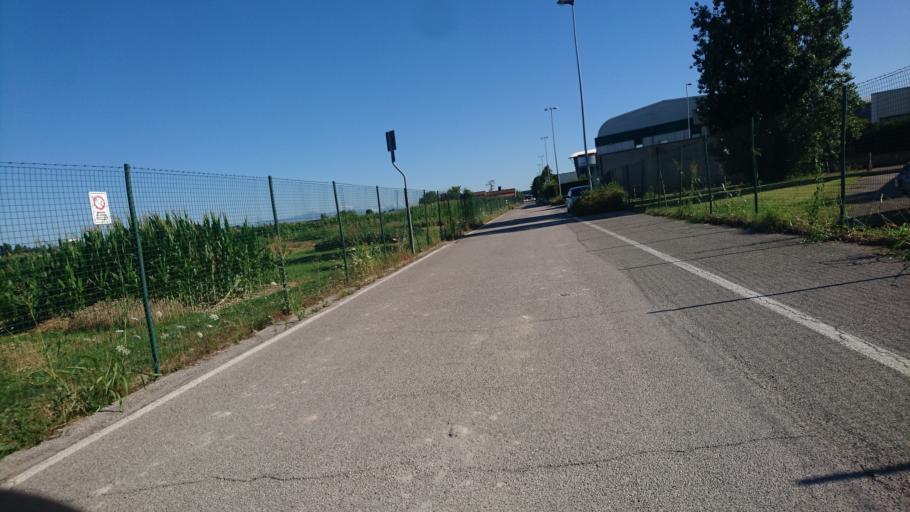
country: IT
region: Veneto
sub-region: Provincia di Padova
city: Legnaro
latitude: 45.3471
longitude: 11.9553
